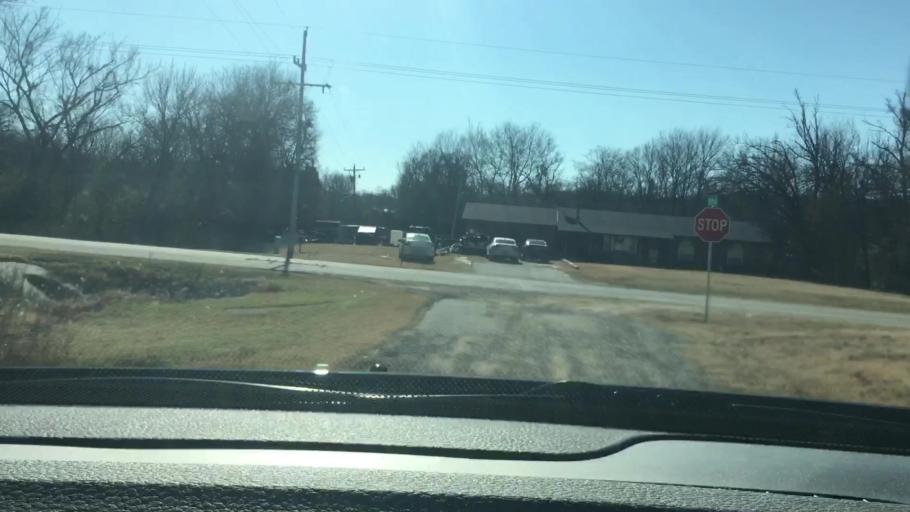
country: US
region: Oklahoma
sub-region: Murray County
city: Davis
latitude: 34.4774
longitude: -97.0448
